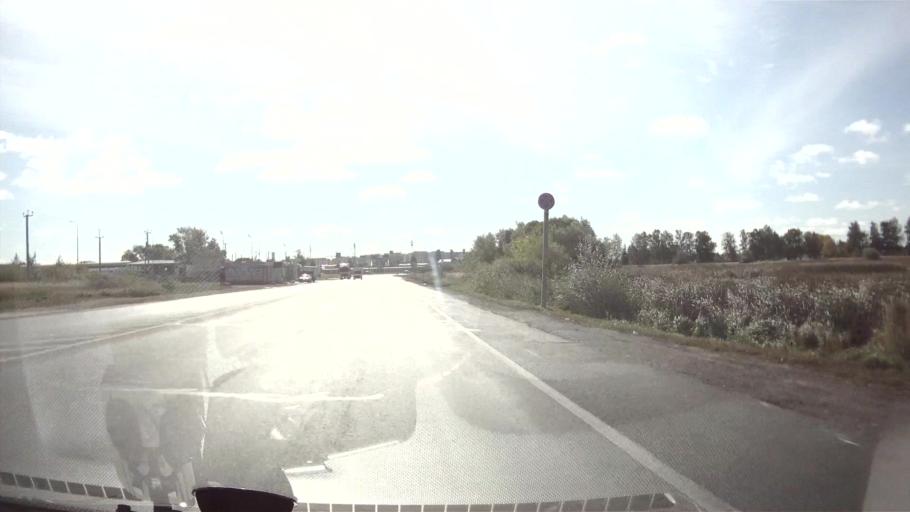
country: RU
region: Ulyanovsk
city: Isheyevka
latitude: 54.2943
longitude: 48.2511
